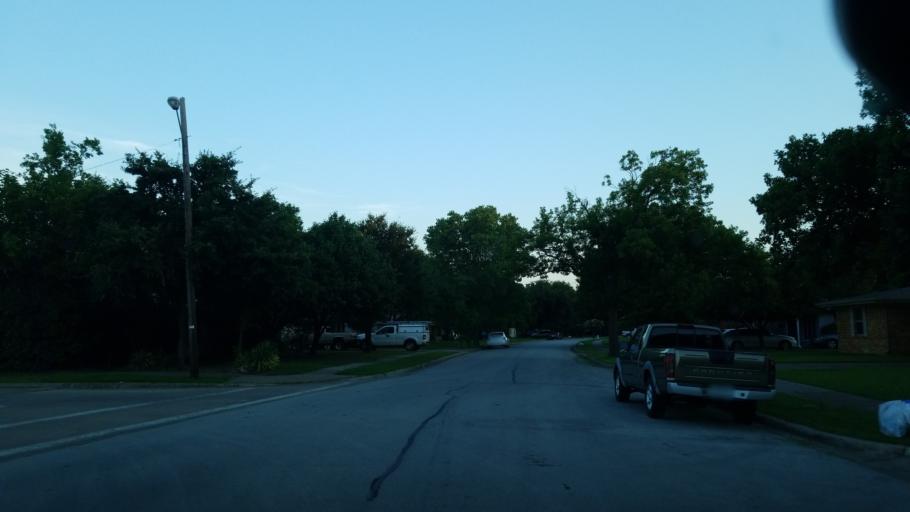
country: US
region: Texas
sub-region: Dallas County
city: Farmers Branch
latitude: 32.9366
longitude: -96.8821
